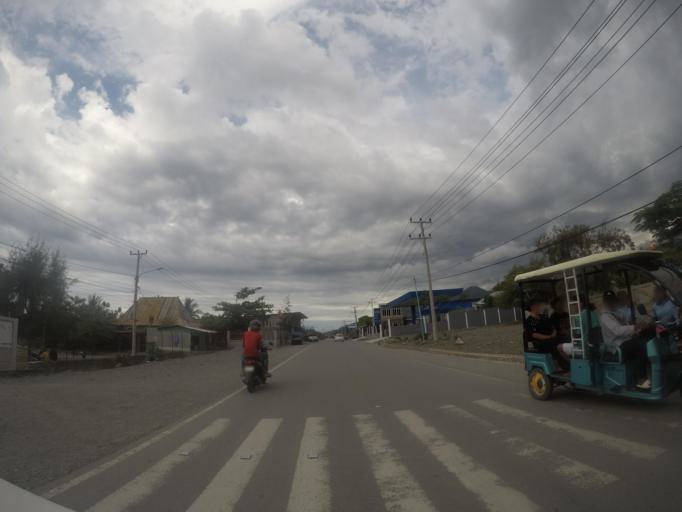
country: TL
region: Liquica
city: Liquica
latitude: -8.5909
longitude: 125.3343
